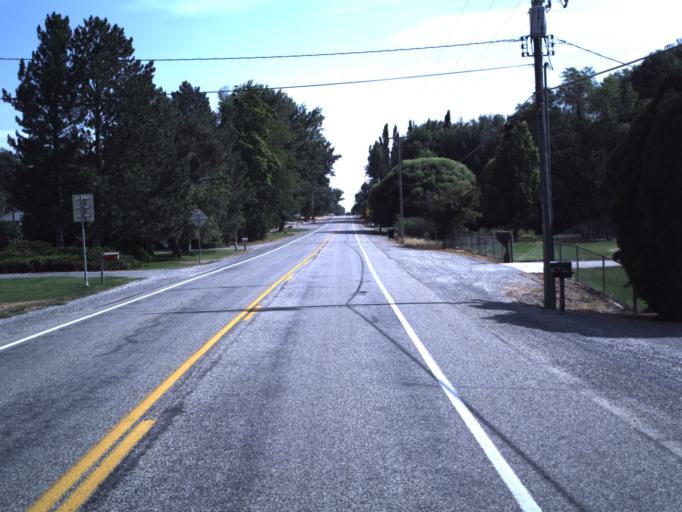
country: US
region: Utah
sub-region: Box Elder County
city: Elwood
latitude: 41.7095
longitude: -112.0902
